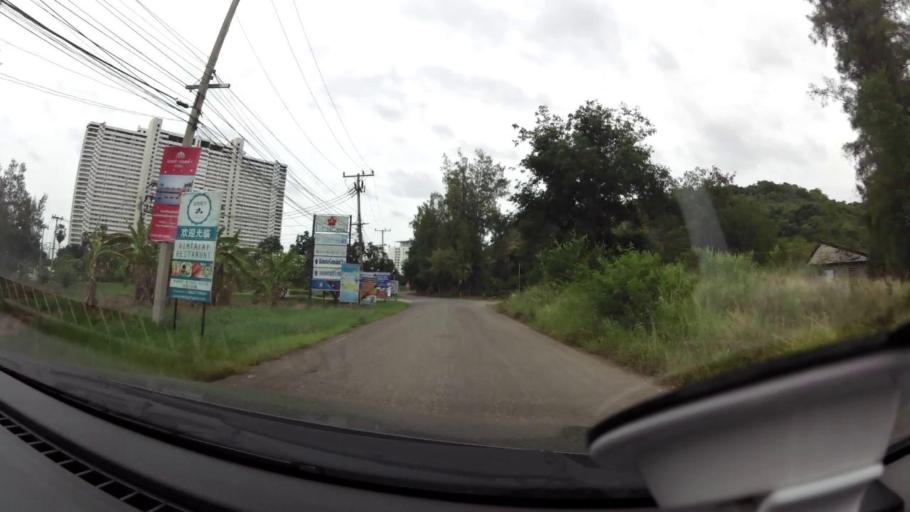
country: TH
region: Prachuap Khiri Khan
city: Pran Buri
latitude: 12.4344
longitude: 99.9766
